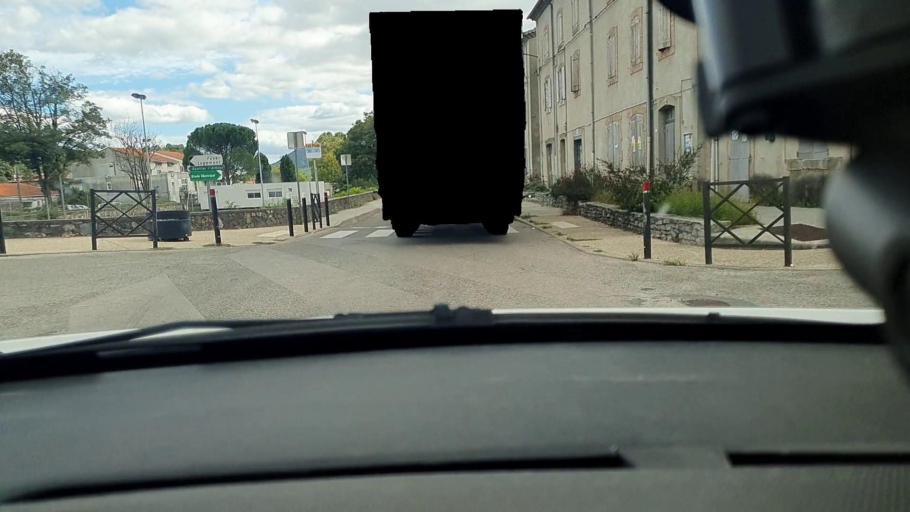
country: FR
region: Languedoc-Roussillon
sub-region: Departement du Gard
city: Saint-Florent-sur-Auzonnet
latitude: 44.2512
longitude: 4.0872
